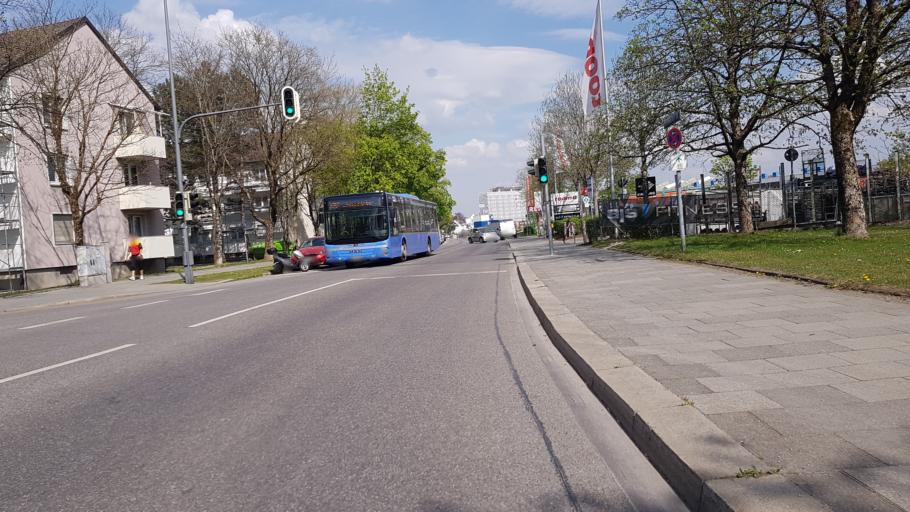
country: DE
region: Bavaria
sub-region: Upper Bavaria
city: Karlsfeld
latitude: 48.1792
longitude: 11.4961
